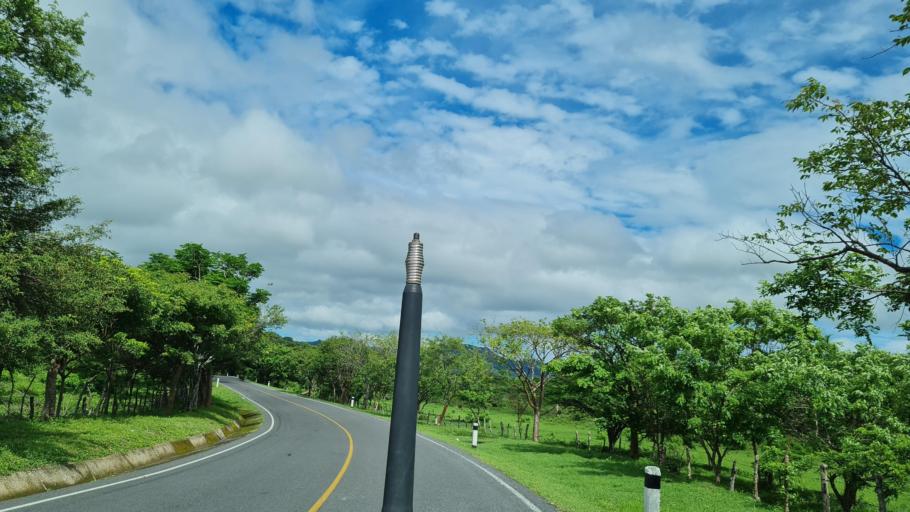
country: NI
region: Boaco
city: San Jose de los Remates
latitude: 12.6132
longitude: -85.8813
